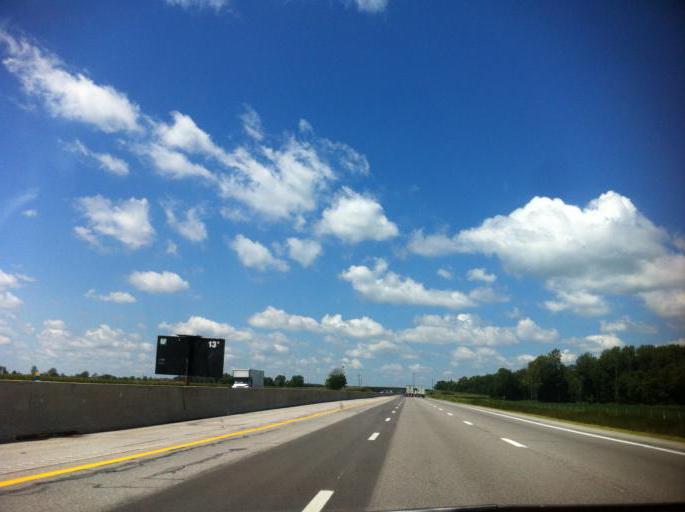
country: US
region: Ohio
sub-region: Ottawa County
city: Elmore
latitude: 41.4392
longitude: -83.2326
